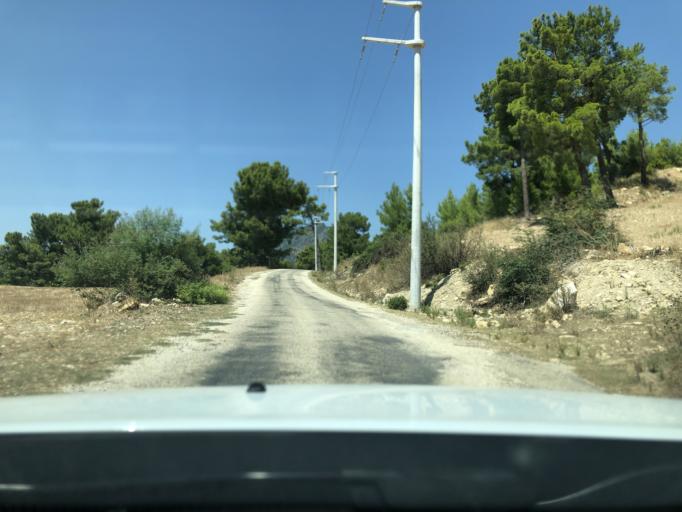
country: TR
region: Antalya
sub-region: Manavgat
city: Manavgat
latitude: 36.8795
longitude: 31.5510
